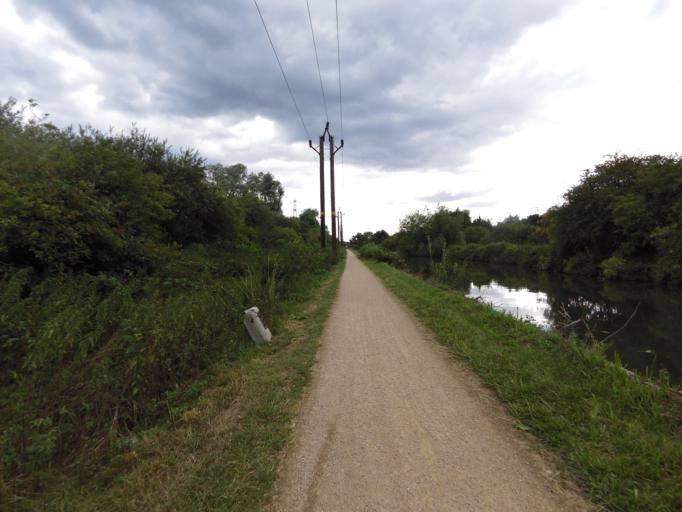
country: GB
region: England
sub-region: Hertfordshire
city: Cheshunt
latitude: 51.7124
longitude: -0.0164
